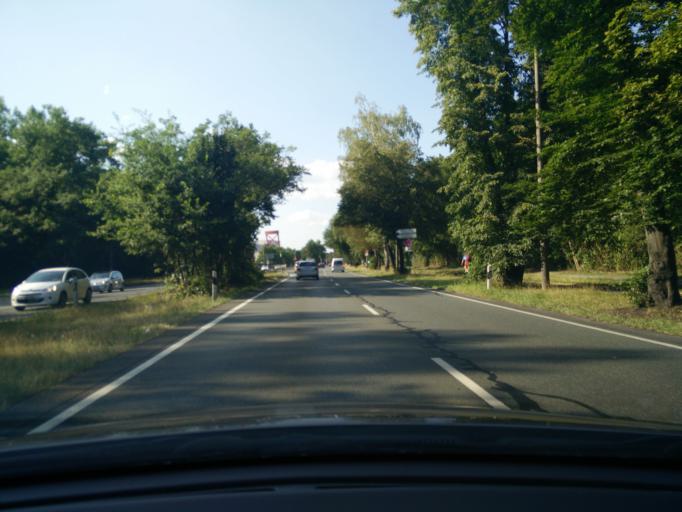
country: DE
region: Bavaria
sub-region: Regierungsbezirk Mittelfranken
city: Nuernberg
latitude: 49.4273
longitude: 11.1041
